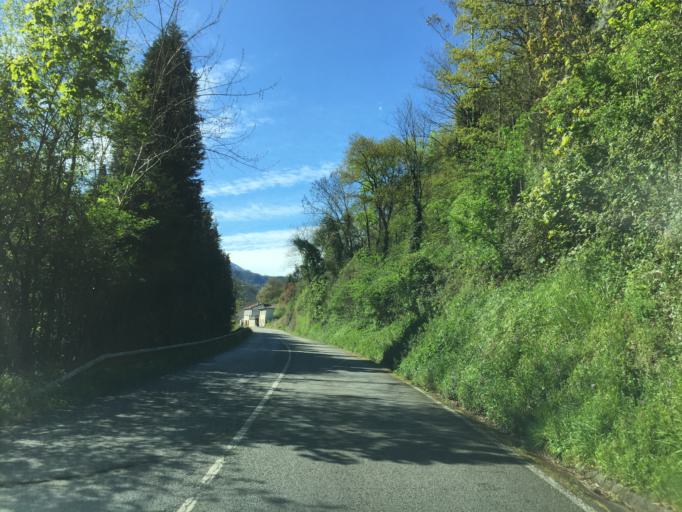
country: ES
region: Asturias
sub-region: Province of Asturias
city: Proaza
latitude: 43.3323
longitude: -5.9879
